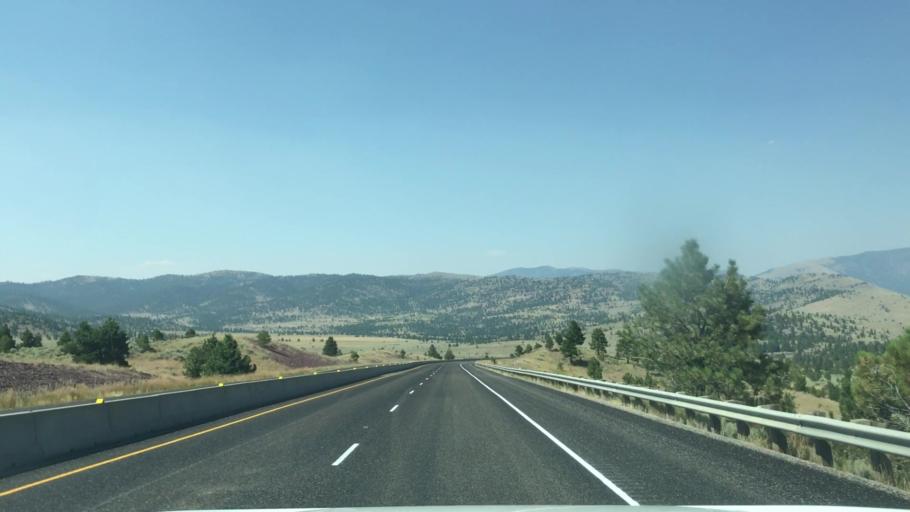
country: US
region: Montana
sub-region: Lewis and Clark County
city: Helena Valley Northwest
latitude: 46.7756
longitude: -112.0341
